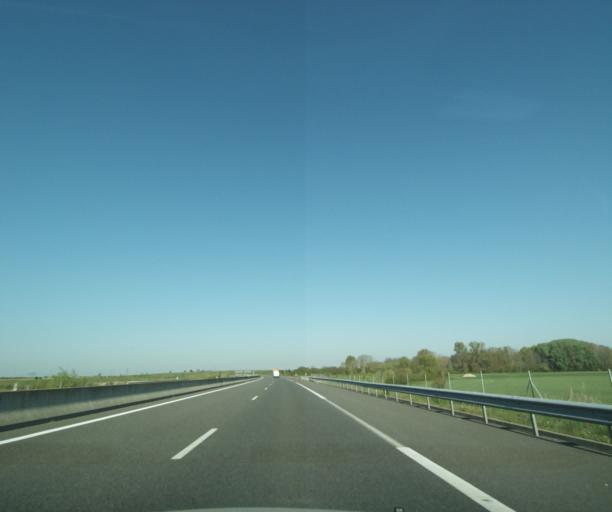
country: FR
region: Centre
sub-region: Departement du Loiret
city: Beaune-la-Rolande
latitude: 48.0938
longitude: 2.4183
